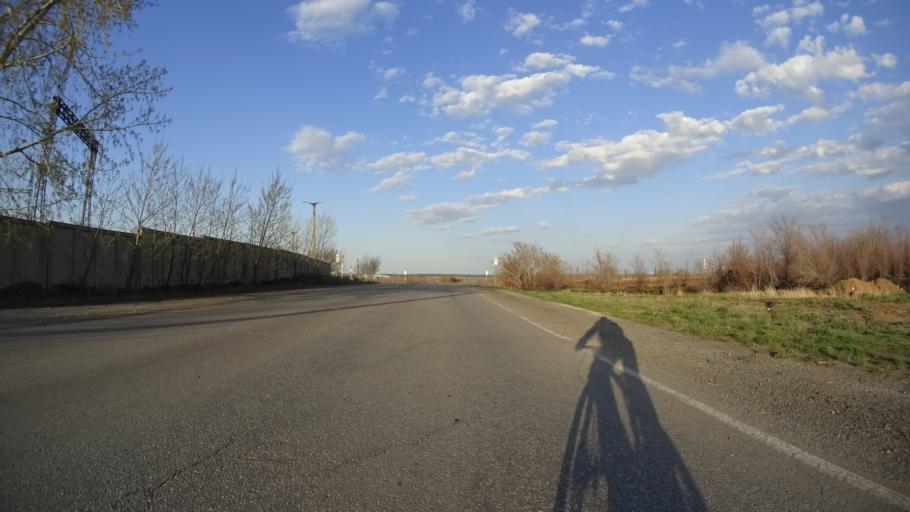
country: RU
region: Chelyabinsk
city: Troitsk
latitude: 54.0623
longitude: 61.5731
